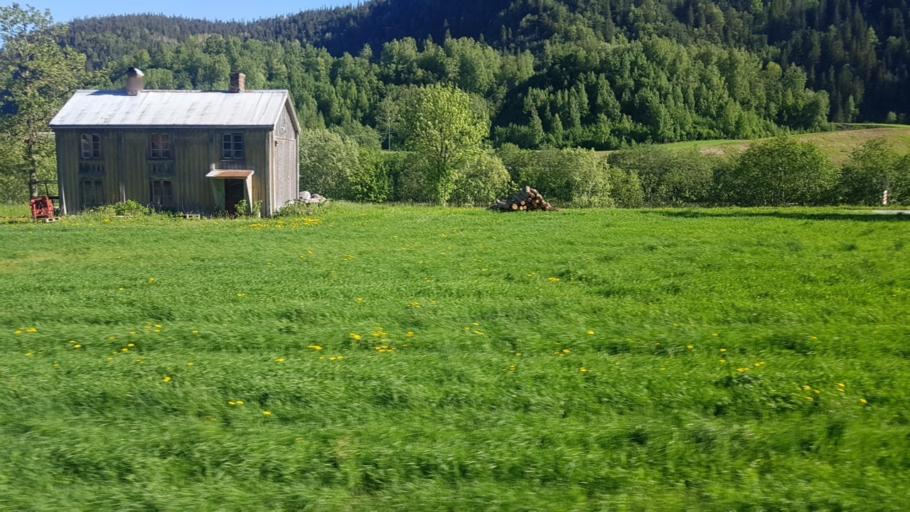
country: NO
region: Sor-Trondelag
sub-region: Midtre Gauldal
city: Storen
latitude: 63.0793
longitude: 10.2597
